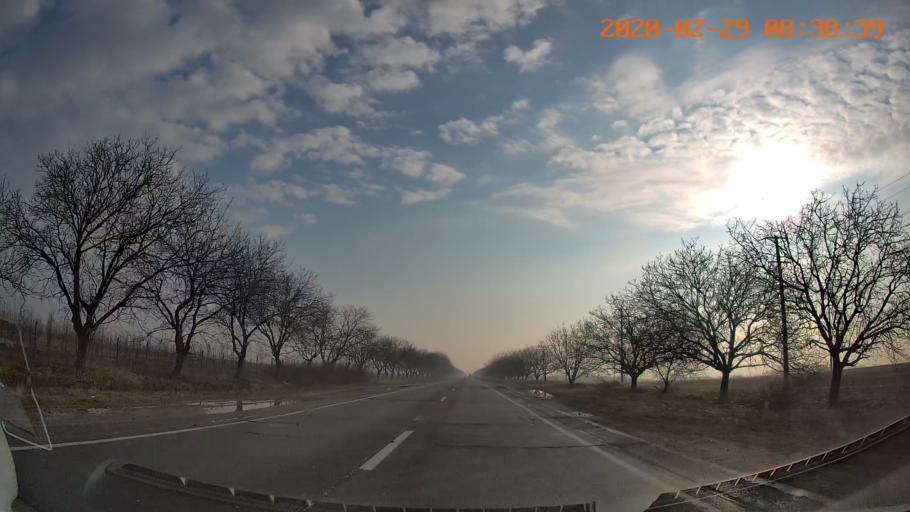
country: MD
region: Anenii Noi
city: Varnita
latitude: 46.9219
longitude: 29.3829
